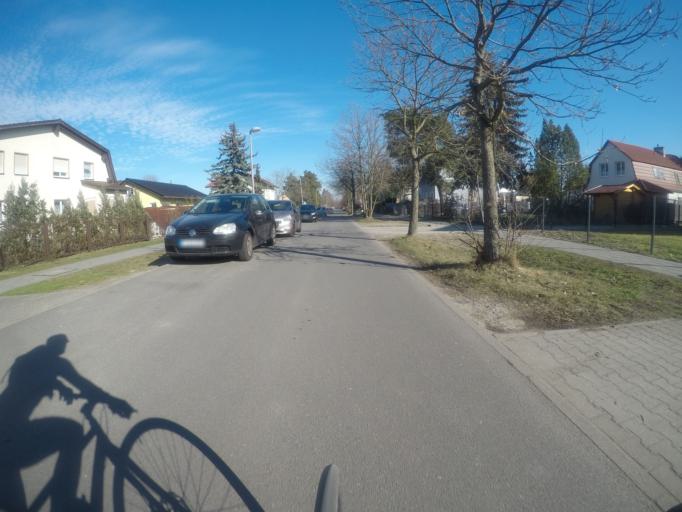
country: DE
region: Berlin
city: Biesdorf
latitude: 52.4988
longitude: 13.5468
